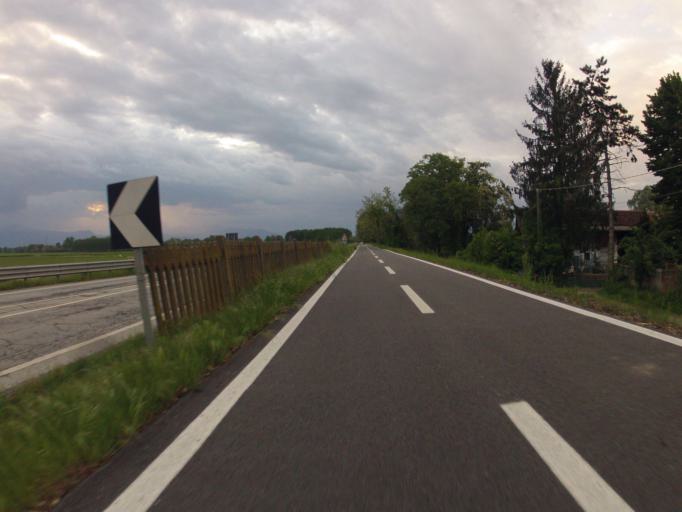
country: IT
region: Piedmont
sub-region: Provincia di Torino
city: Villafranca Piemonte
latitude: 44.8070
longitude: 7.5017
